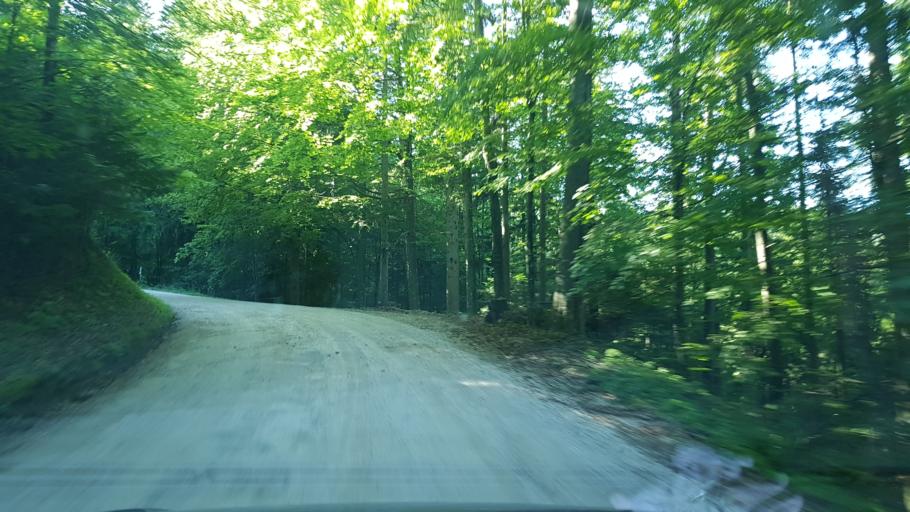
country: SI
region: Ravne na Koroskem
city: Kotlje
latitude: 46.4992
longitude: 14.9517
